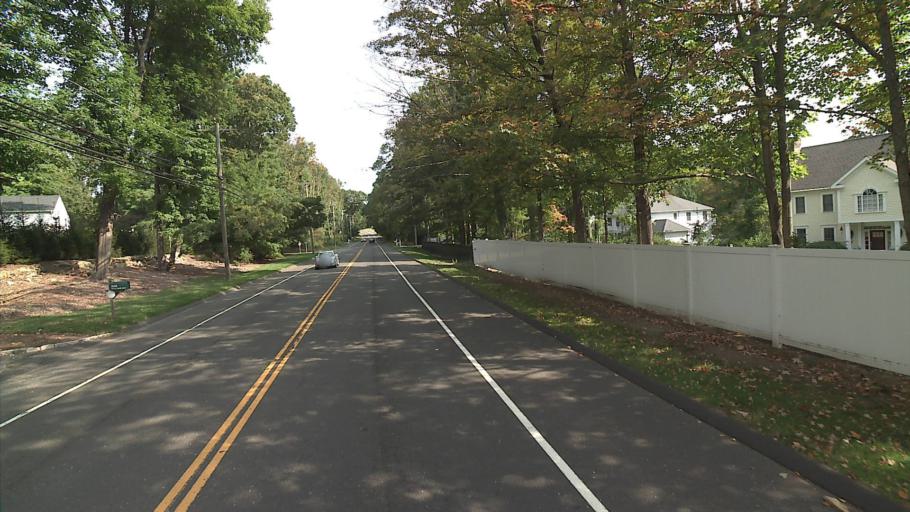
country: US
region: Connecticut
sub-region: Fairfield County
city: New Canaan
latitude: 41.1653
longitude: -73.4952
